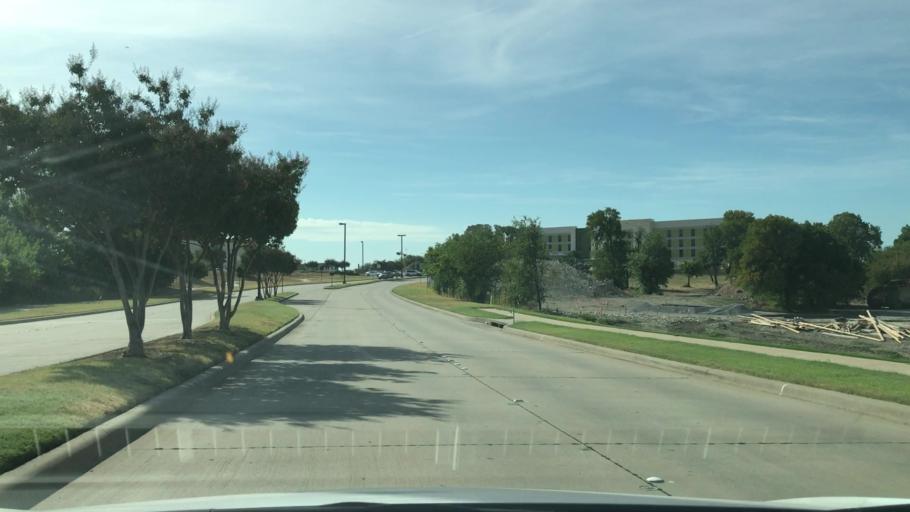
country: US
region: Texas
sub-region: Denton County
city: The Colony
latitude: 33.0724
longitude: -96.8361
